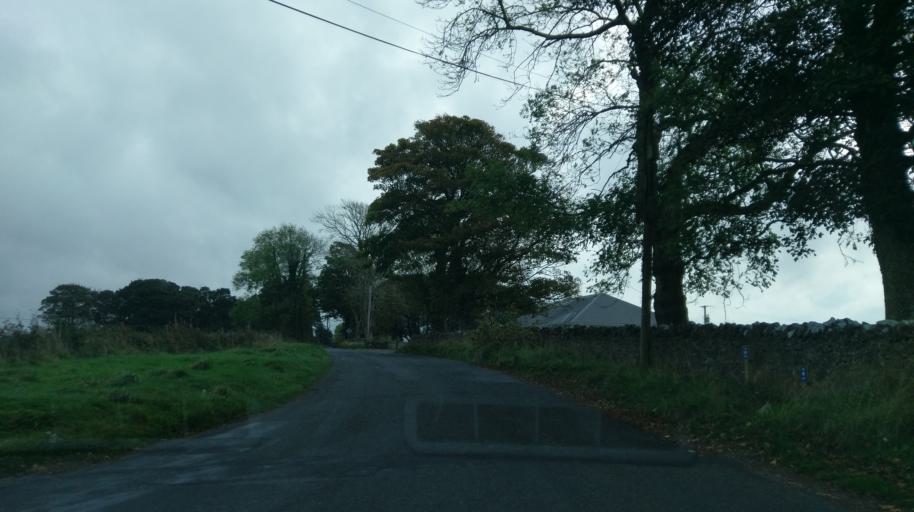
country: IE
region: Connaught
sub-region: County Galway
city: Athenry
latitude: 53.4535
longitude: -8.5849
